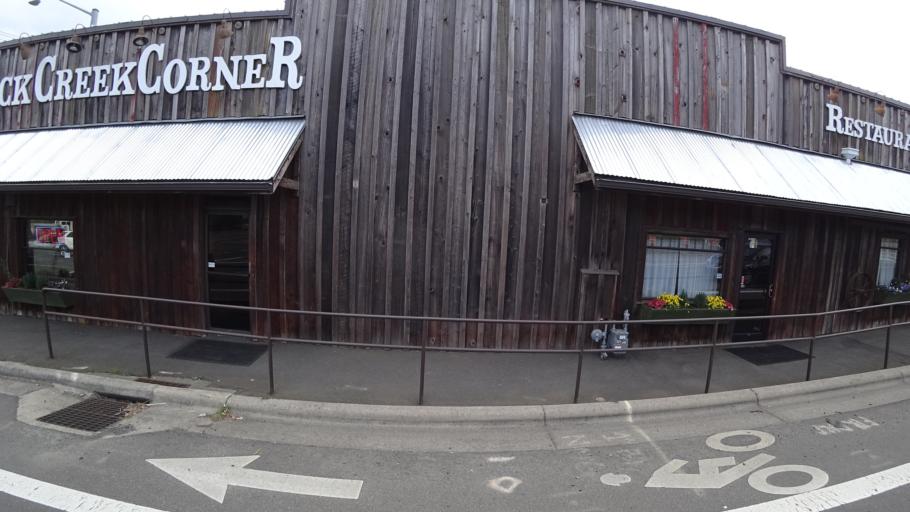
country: US
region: Oregon
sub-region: Washington County
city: Bethany
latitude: 45.5583
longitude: -122.8677
